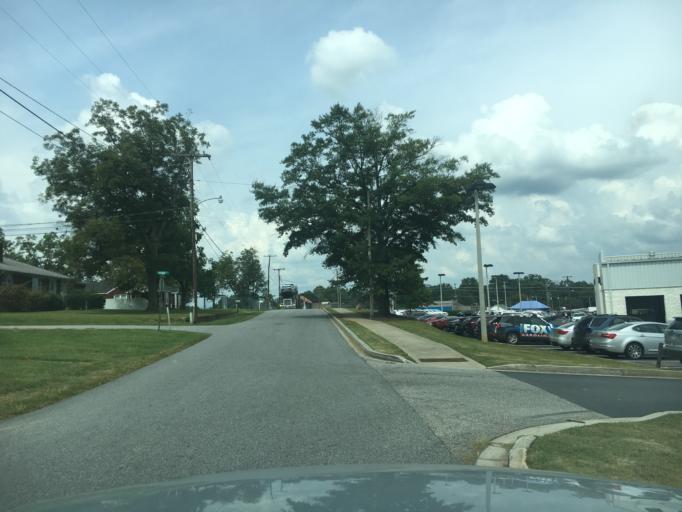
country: US
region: South Carolina
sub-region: Greenville County
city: Greer
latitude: 34.9460
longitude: -82.2168
